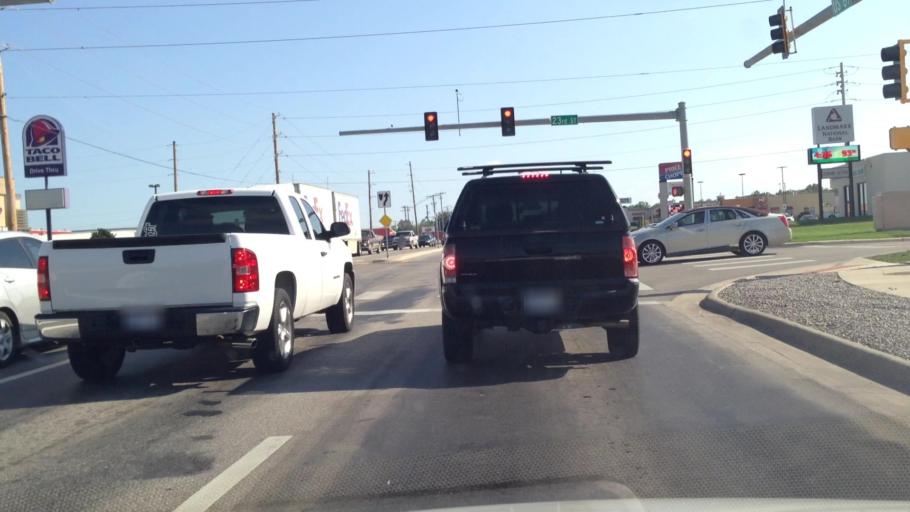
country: US
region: Kansas
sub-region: Bourbon County
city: Fort Scott
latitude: 37.8132
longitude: -94.7055
